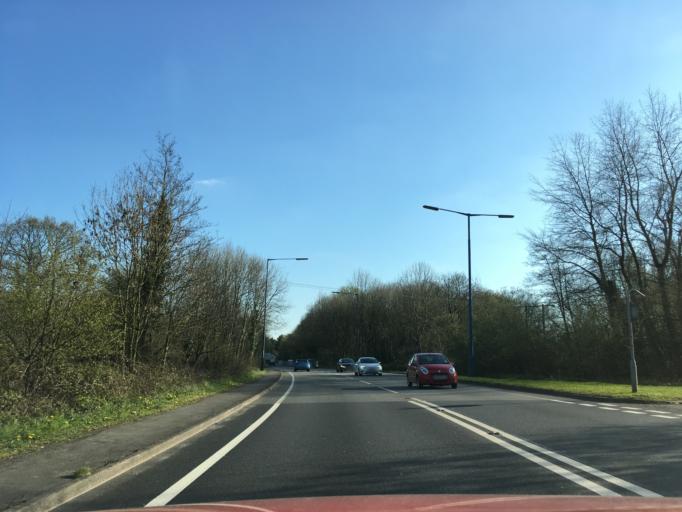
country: GB
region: Wales
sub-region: Torfaen County Borough
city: New Inn
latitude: 51.6797
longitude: -3.0157
